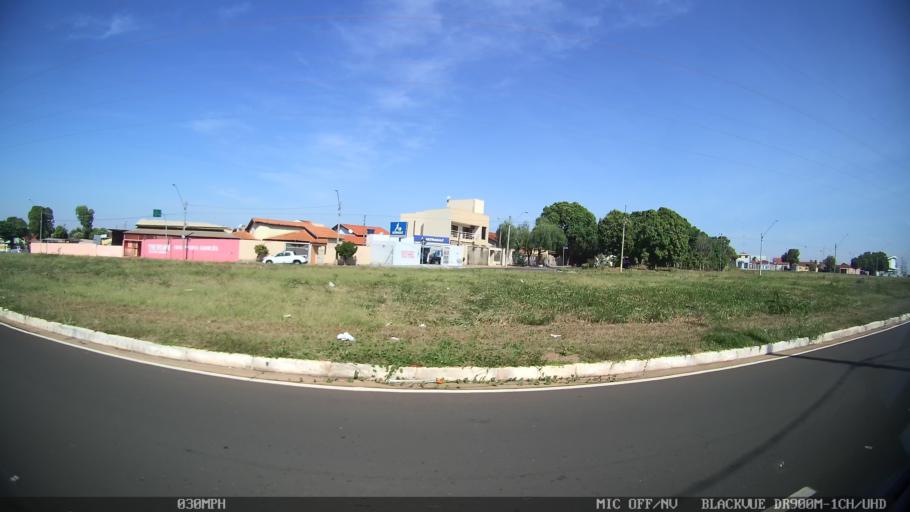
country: BR
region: Sao Paulo
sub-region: Sao Jose Do Rio Preto
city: Sao Jose do Rio Preto
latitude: -20.7896
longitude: -49.4183
